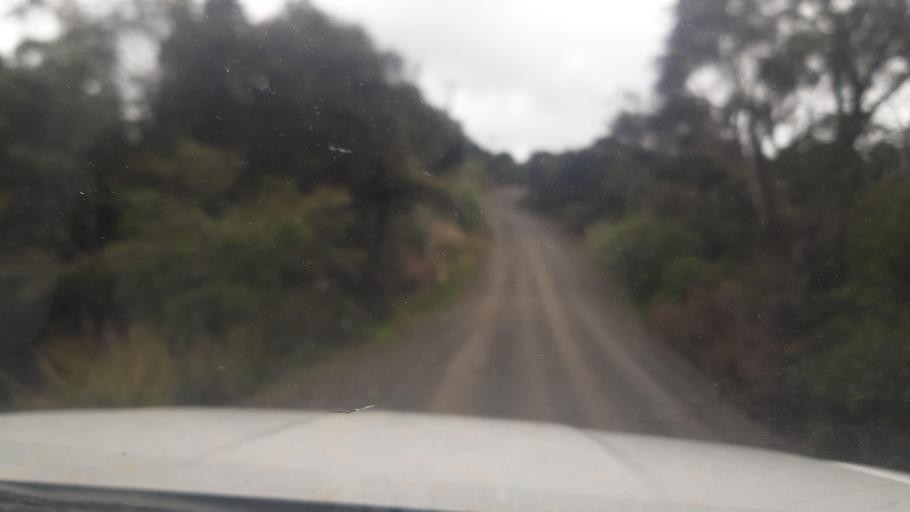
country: NZ
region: Northland
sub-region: Far North District
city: Taipa
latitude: -35.0613
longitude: 173.5329
